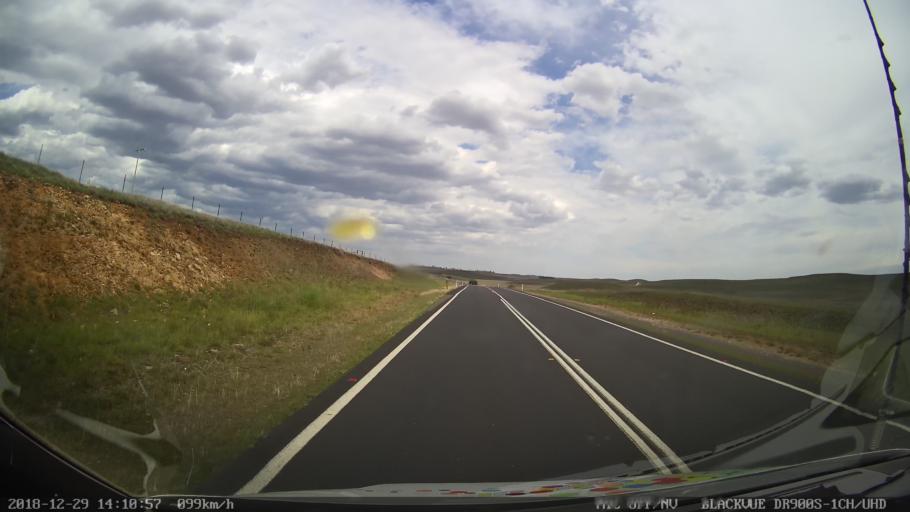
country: AU
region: New South Wales
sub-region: Cooma-Monaro
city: Cooma
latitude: -36.3991
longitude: 149.2174
